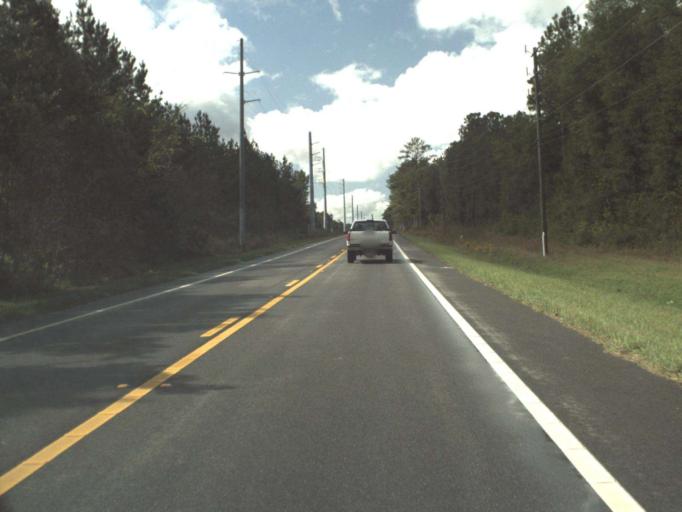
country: US
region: Florida
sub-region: Gadsden County
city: Midway
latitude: 30.3939
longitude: -84.6148
